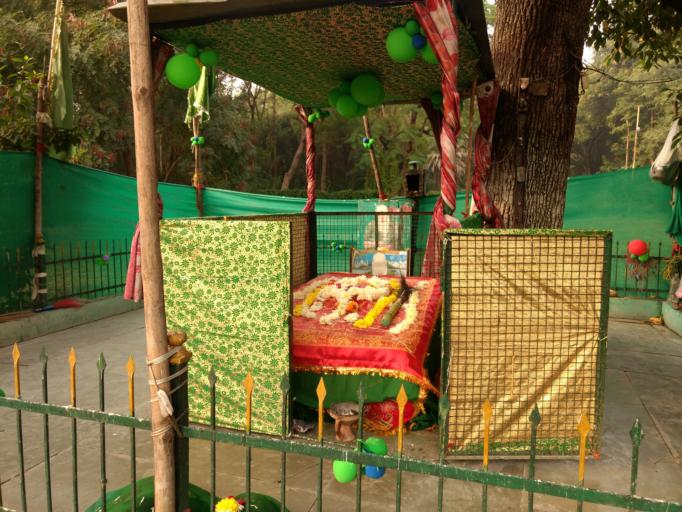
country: IN
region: Maharashtra
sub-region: Nagpur Division
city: Nagpur
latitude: 21.1552
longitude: 79.0492
